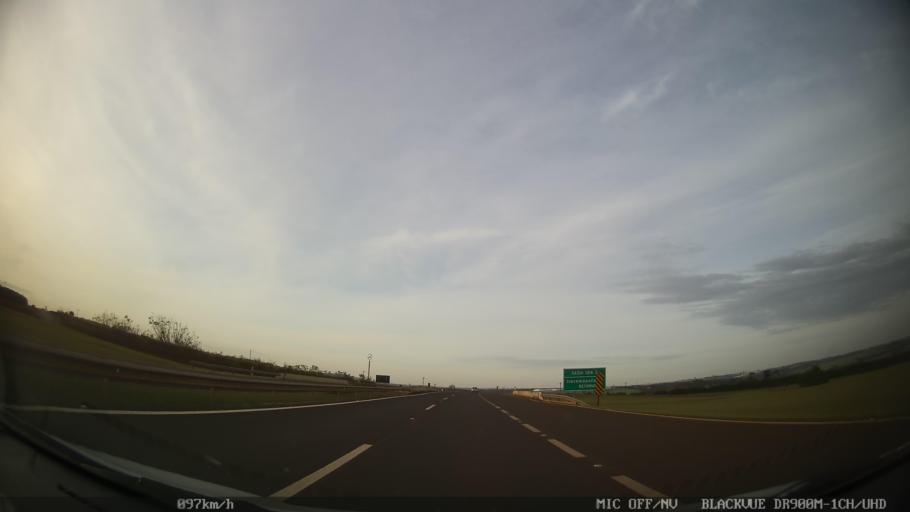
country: BR
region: Sao Paulo
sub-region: Iracemapolis
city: Iracemapolis
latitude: -22.6319
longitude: -47.5051
